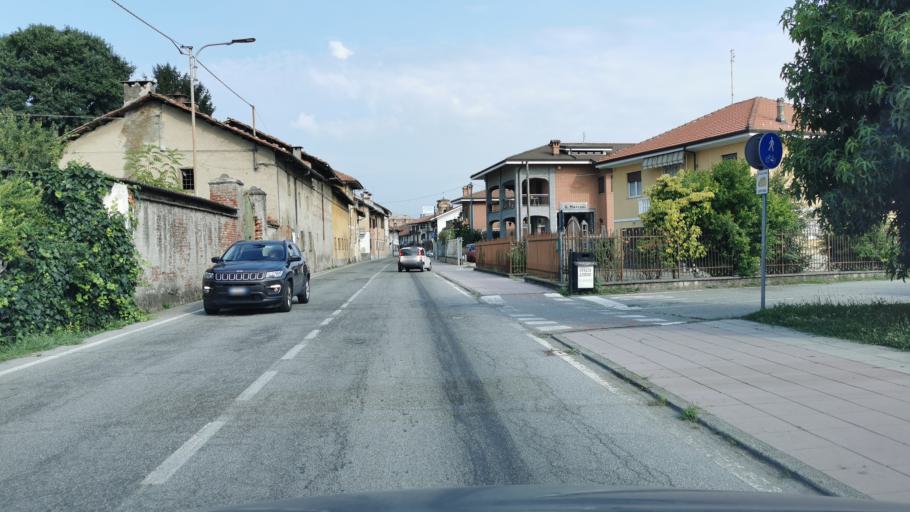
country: IT
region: Piedmont
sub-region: Provincia di Torino
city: Vigone
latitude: 44.8412
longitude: 7.5017
